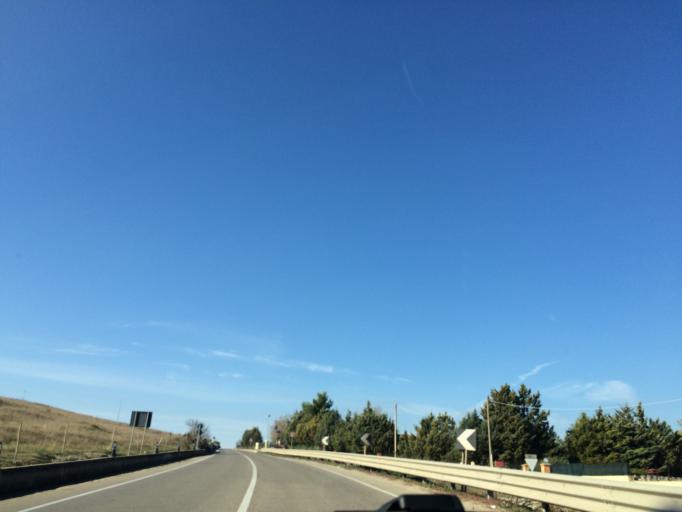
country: IT
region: Basilicate
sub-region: Provincia di Matera
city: Matera
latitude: 40.6796
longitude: 16.6260
